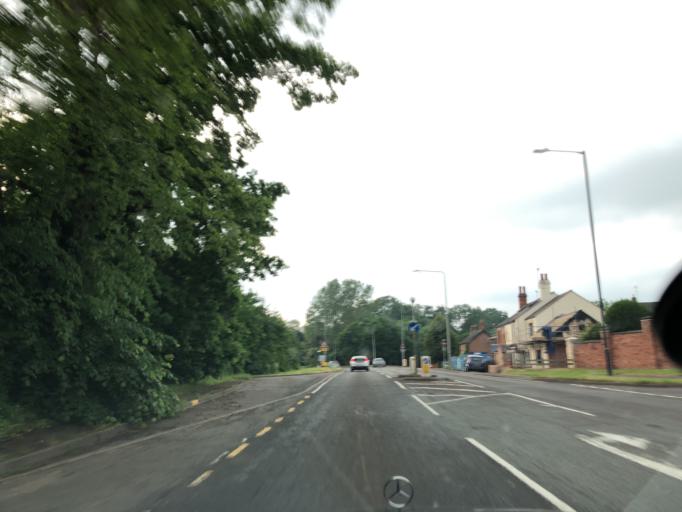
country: GB
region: England
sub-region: Warwickshire
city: Wroxall
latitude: 52.2989
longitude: -1.6371
